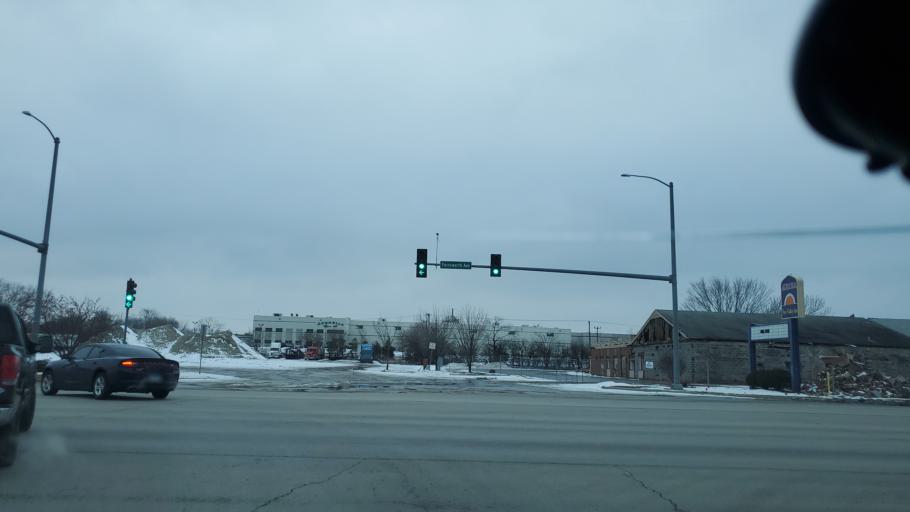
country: US
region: Illinois
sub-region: Kane County
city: North Aurora
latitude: 41.8041
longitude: -88.2819
